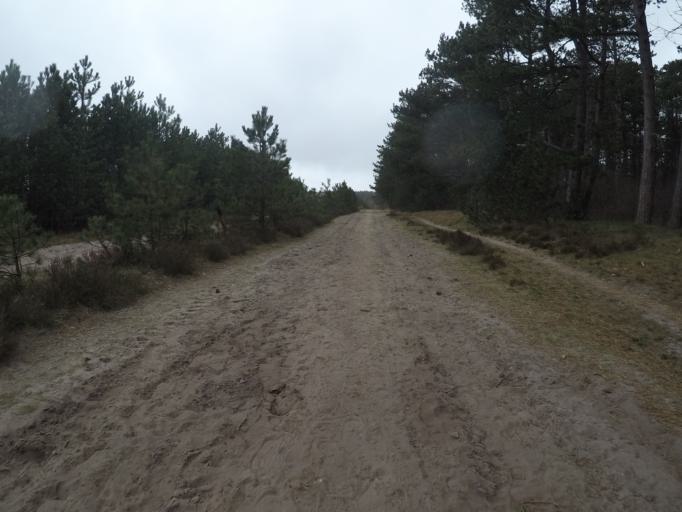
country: DE
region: Lower Saxony
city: Nordholz
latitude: 53.8260
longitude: 8.6445
